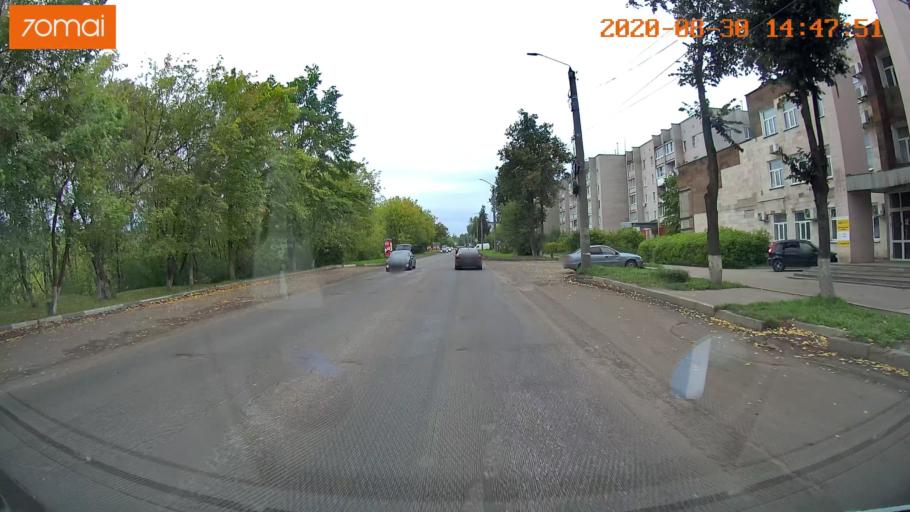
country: RU
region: Ivanovo
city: Kineshma
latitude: 57.4379
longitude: 42.1281
